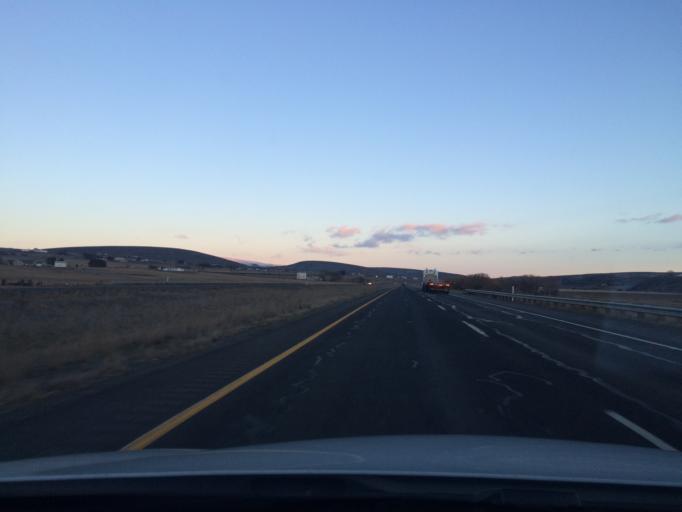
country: US
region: Washington
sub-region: Kittitas County
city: Kittitas
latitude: 46.9722
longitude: -120.3909
